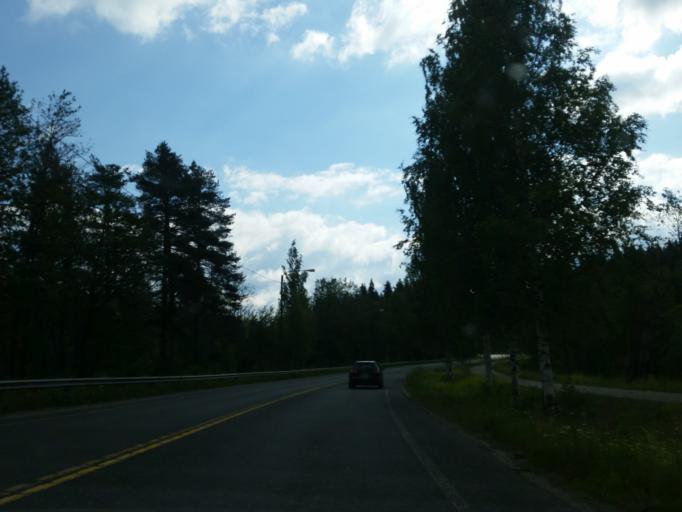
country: FI
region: Northern Savo
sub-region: Kuopio
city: Kuopio
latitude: 62.8403
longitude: 27.5864
